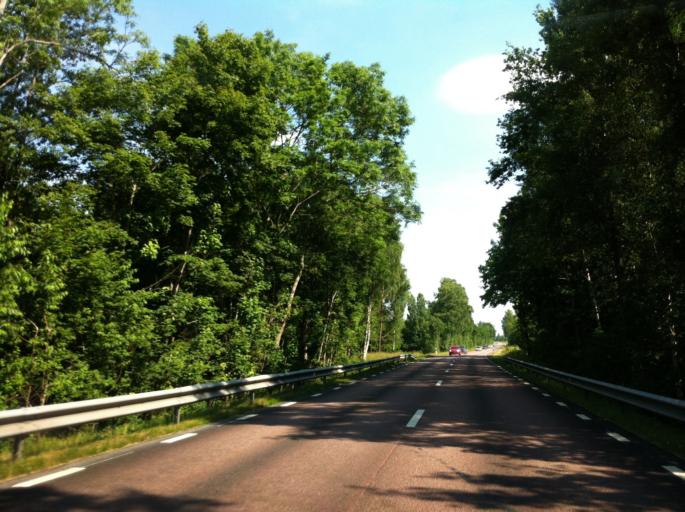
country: SE
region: Kalmar
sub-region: Nybro Kommun
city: Nybro
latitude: 56.7884
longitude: 15.7987
